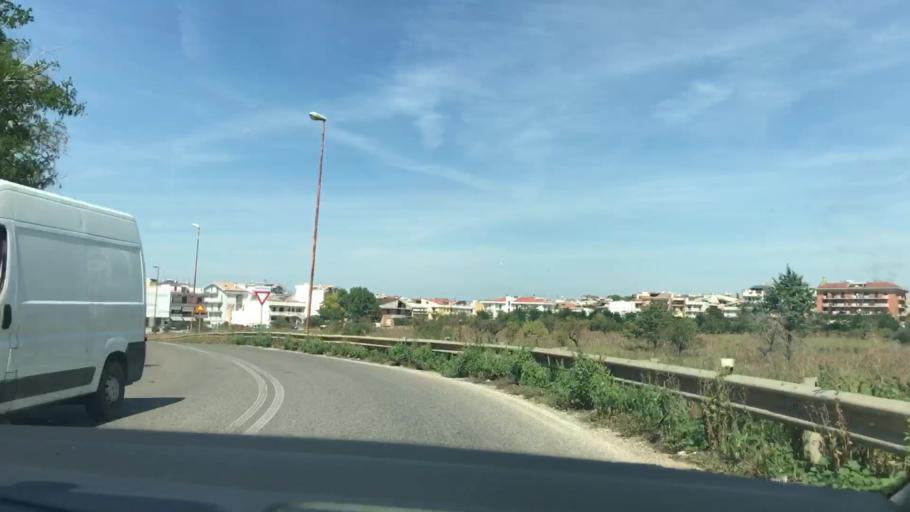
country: IT
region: Apulia
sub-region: Provincia di Bari
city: Altamura
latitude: 40.8151
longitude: 16.5560
